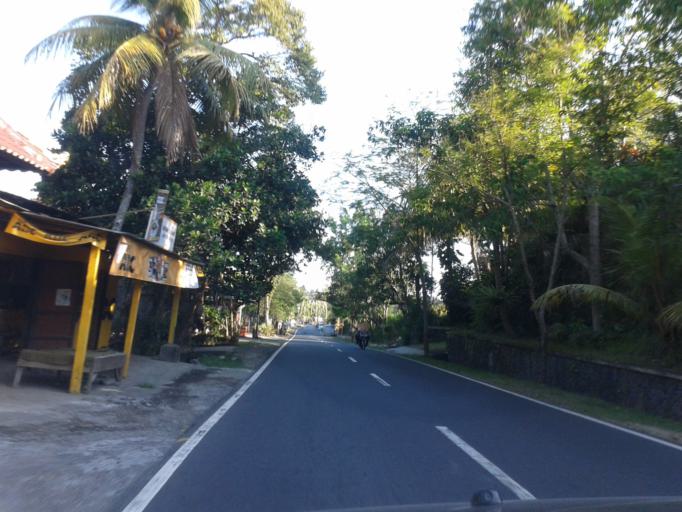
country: ID
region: Bali
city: Banjar Wangsian
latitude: -8.4914
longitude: 115.4023
